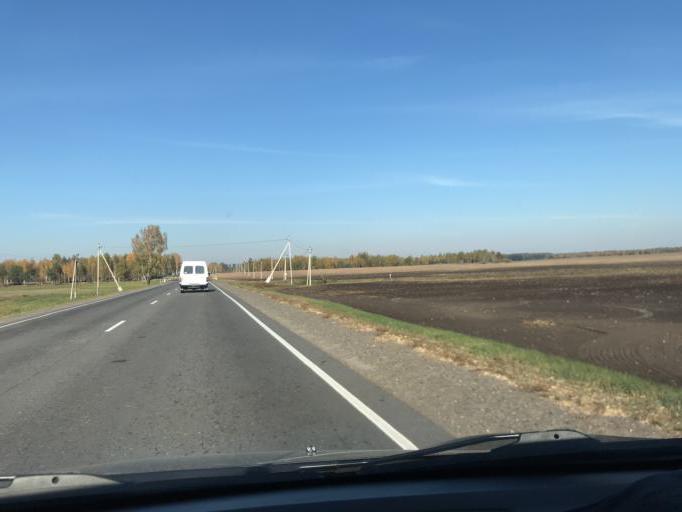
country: BY
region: Gomel
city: Parychy
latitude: 52.6677
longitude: 29.3603
